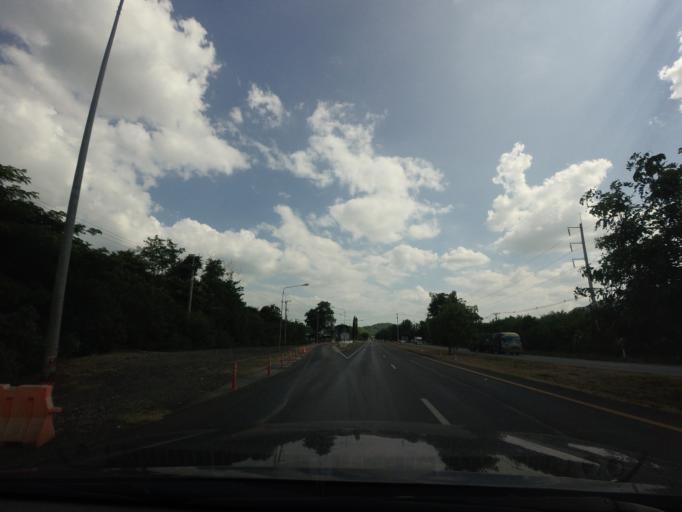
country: TH
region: Phetchabun
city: Wichian Buri
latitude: 15.6389
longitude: 101.0450
